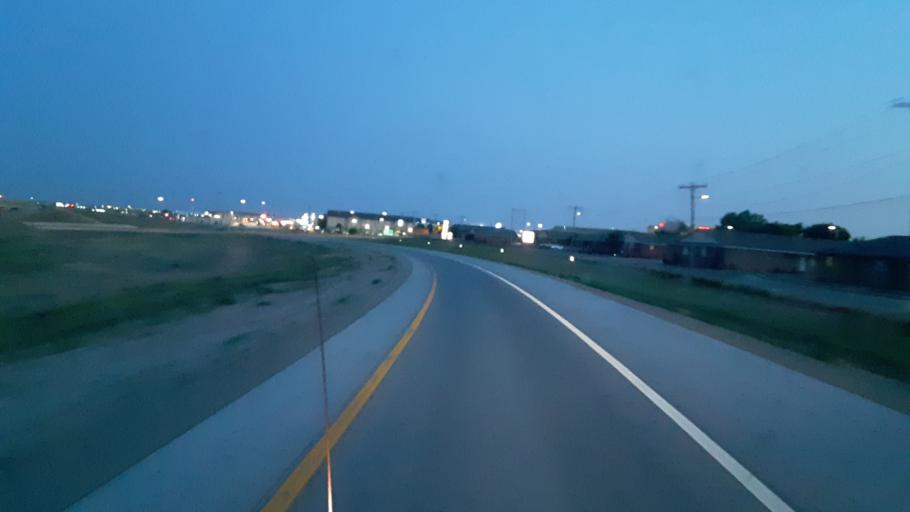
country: US
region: Kansas
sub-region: Finney County
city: Garden City
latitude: 37.9848
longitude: -100.8393
